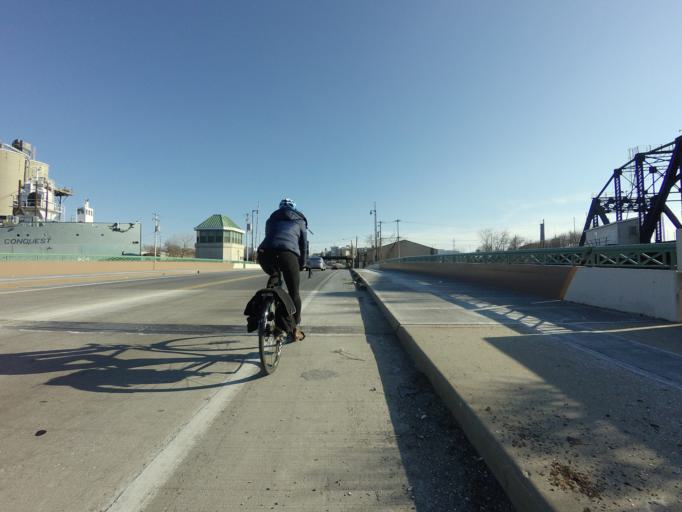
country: US
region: Wisconsin
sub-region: Milwaukee County
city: Milwaukee
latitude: 43.0085
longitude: -87.9086
